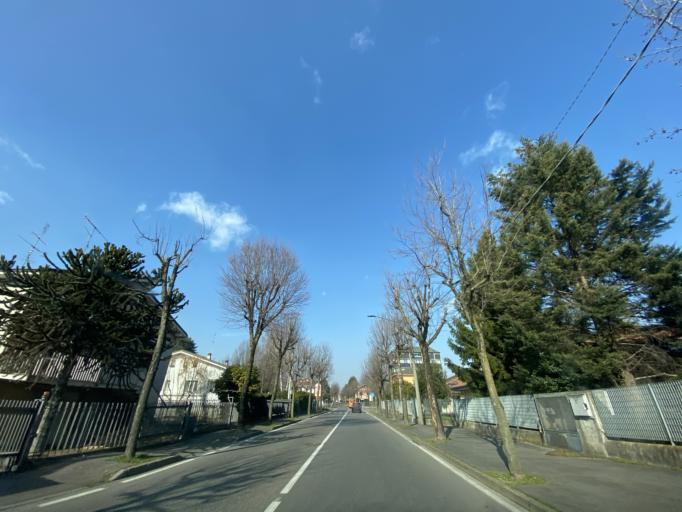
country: IT
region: Lombardy
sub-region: Provincia di Varese
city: Saronno
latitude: 45.6182
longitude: 9.0462
